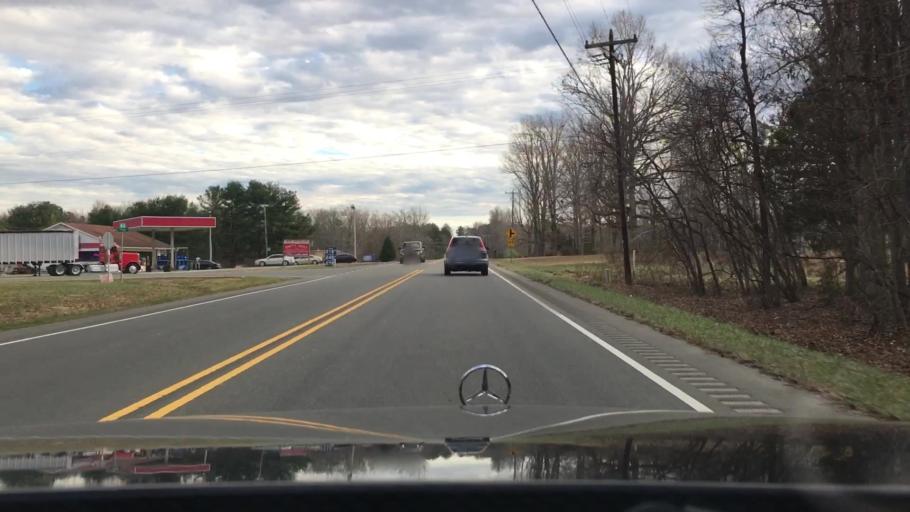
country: US
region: North Carolina
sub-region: Orange County
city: Hillsborough
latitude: 36.1373
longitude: -79.1207
